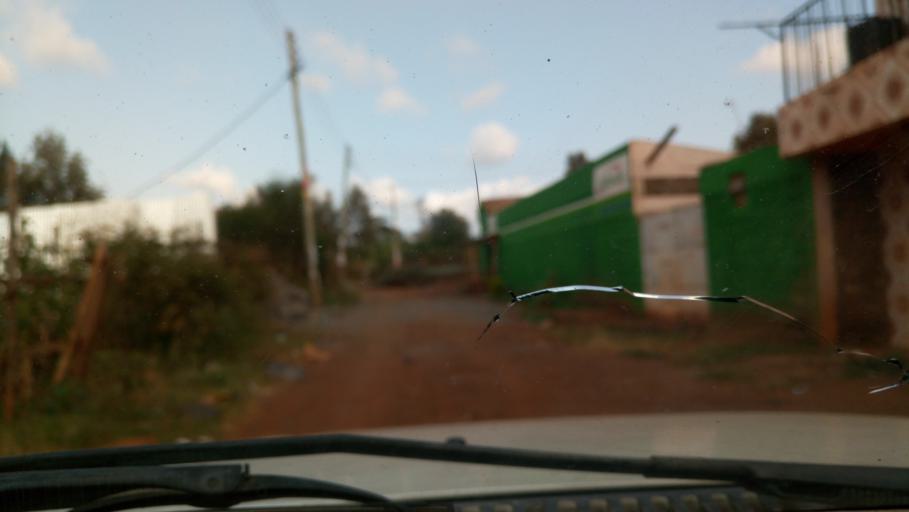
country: KE
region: Nairobi Area
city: Thika
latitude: -0.9330
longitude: 37.1247
